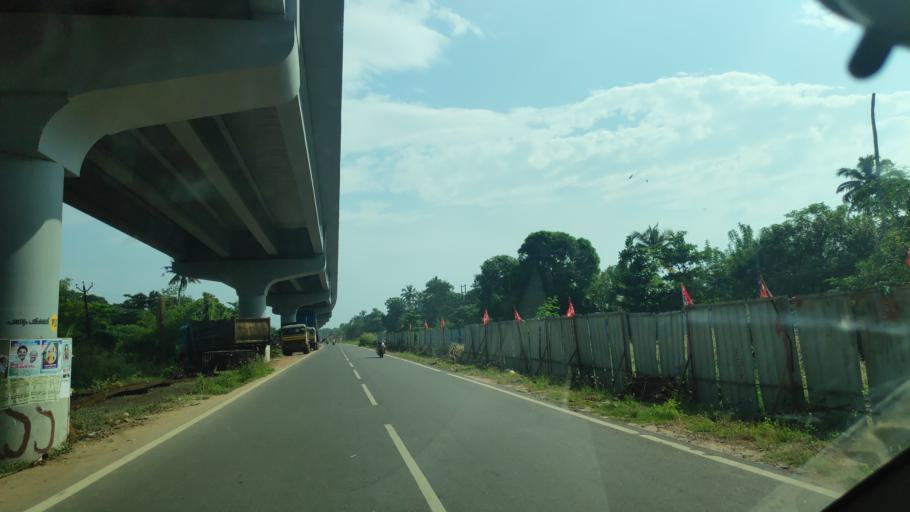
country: IN
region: Kerala
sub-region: Alappuzha
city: Alleppey
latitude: 9.4805
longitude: 76.3216
